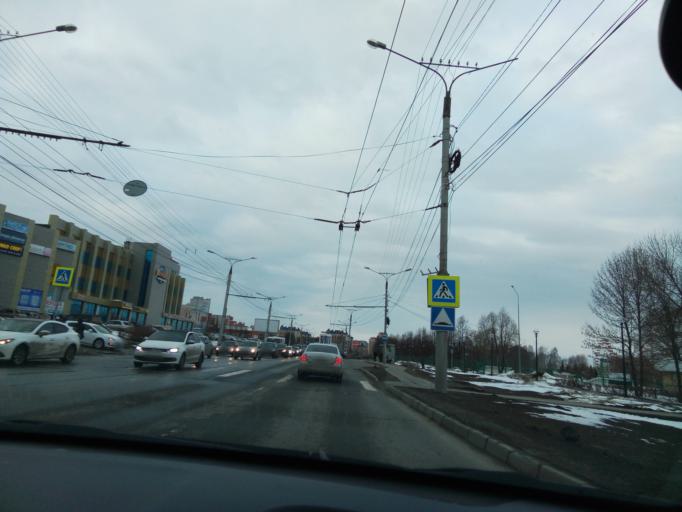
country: RU
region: Chuvashia
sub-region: Cheboksarskiy Rayon
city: Cheboksary
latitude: 56.1446
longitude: 47.2051
